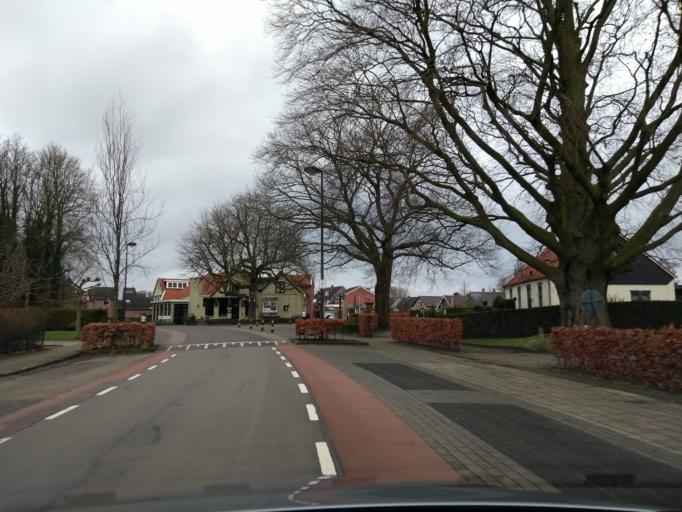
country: NL
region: Overijssel
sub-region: Gemeente Haaksbergen
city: Haaksbergen
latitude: 52.1459
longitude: 6.8304
